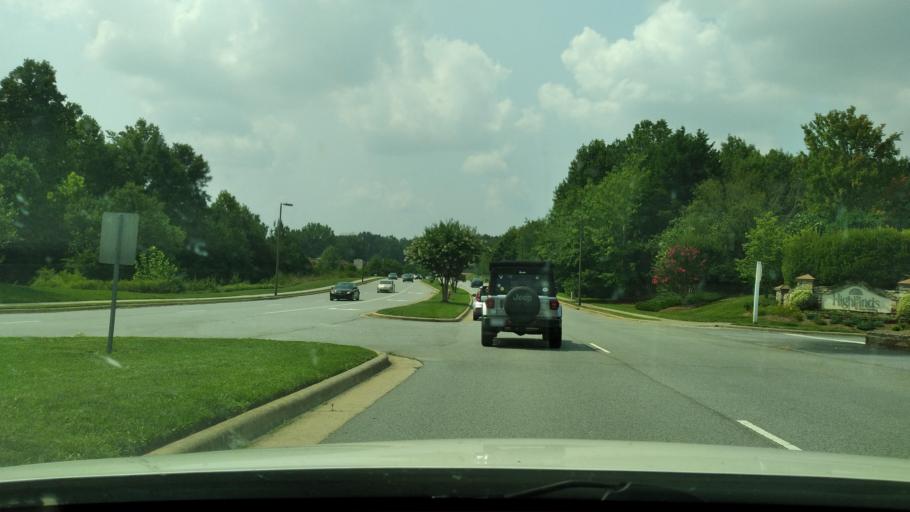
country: US
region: North Carolina
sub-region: Guilford County
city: Jamestown
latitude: 36.0425
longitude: -79.9243
